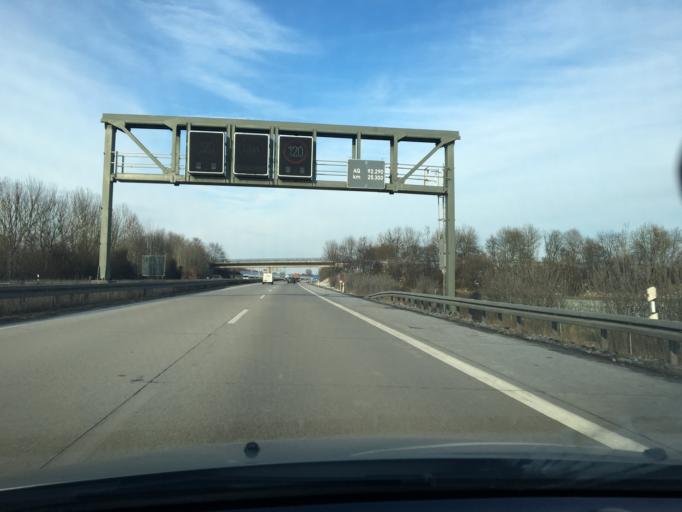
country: DE
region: Bavaria
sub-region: Upper Bavaria
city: Freising
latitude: 48.3742
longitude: 11.7486
